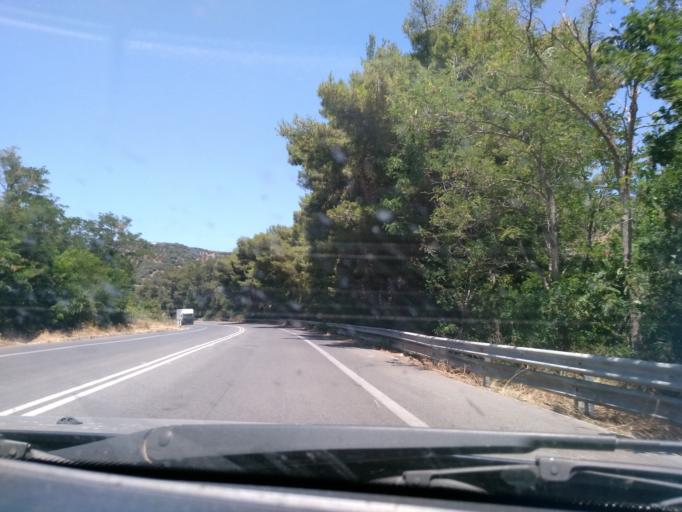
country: GR
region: Crete
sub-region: Nomos Rethymnis
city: Anogeia
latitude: 35.3966
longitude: 24.8784
